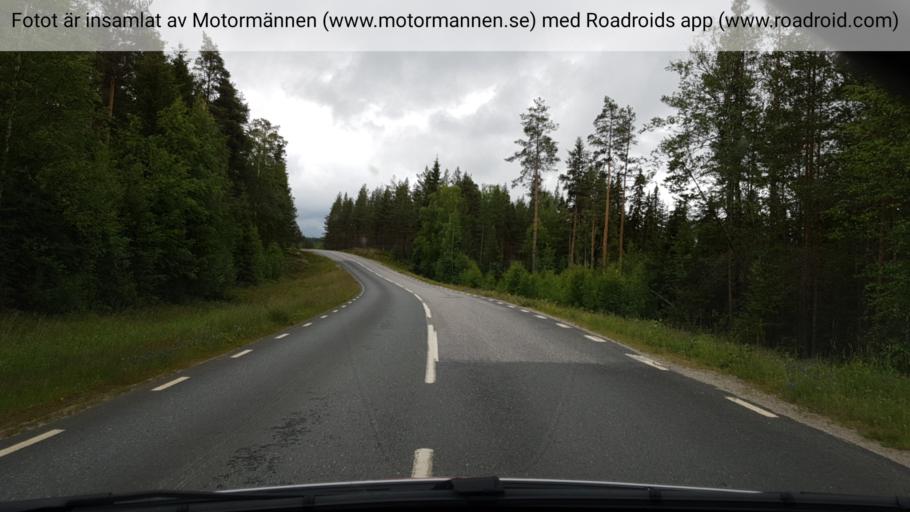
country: SE
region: Vaesterbotten
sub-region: Norsjo Kommun
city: Norsjoe
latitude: 64.6364
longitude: 19.2864
